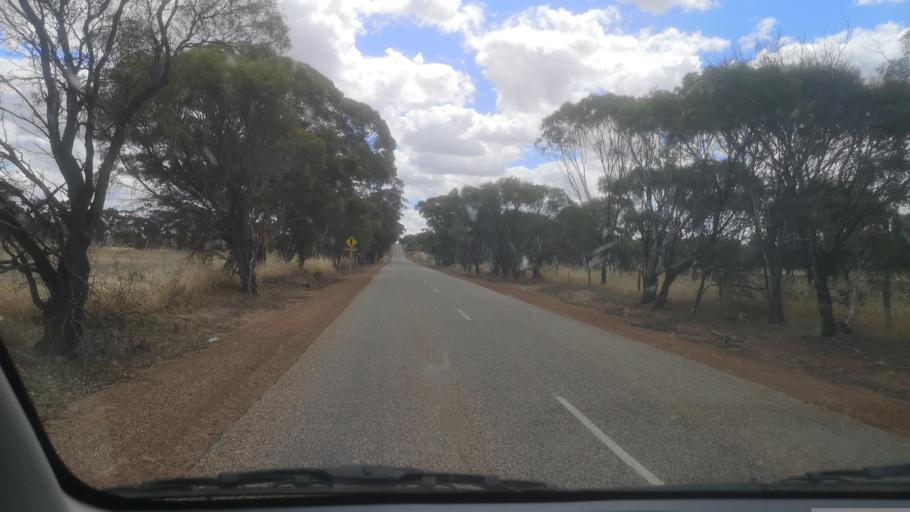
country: AU
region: Western Australia
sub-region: Beverley
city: Beverley
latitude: -31.9899
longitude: 117.1236
